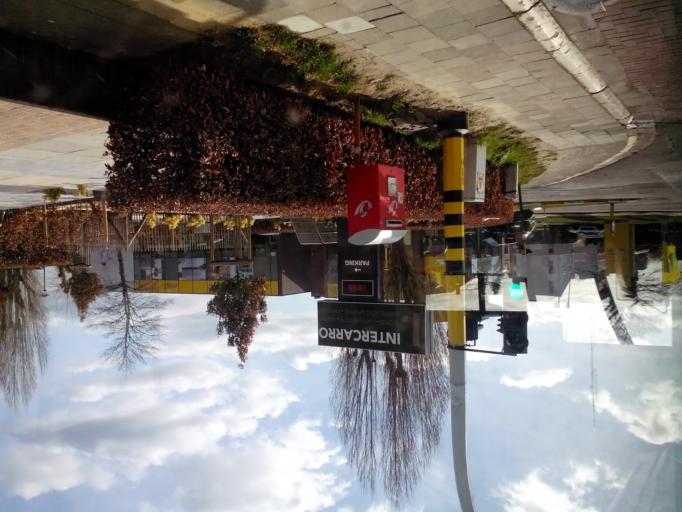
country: BE
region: Flanders
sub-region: Provincie Vlaams-Brabant
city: Diegem
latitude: 50.8641
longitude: 4.4341
